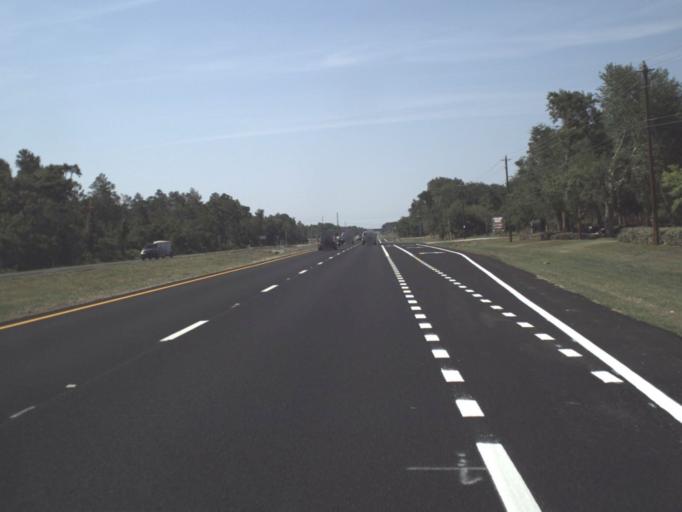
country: US
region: Florida
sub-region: Brevard County
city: Port Saint John
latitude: 28.5194
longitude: -80.7867
